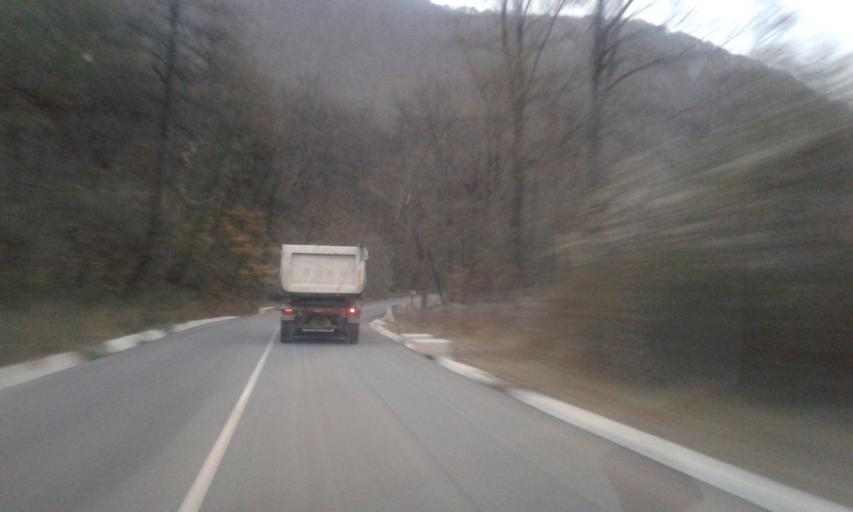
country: RO
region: Gorj
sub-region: Comuna Bumbesti-Jiu
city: Bumbesti-Jiu
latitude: 45.2140
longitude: 23.3810
